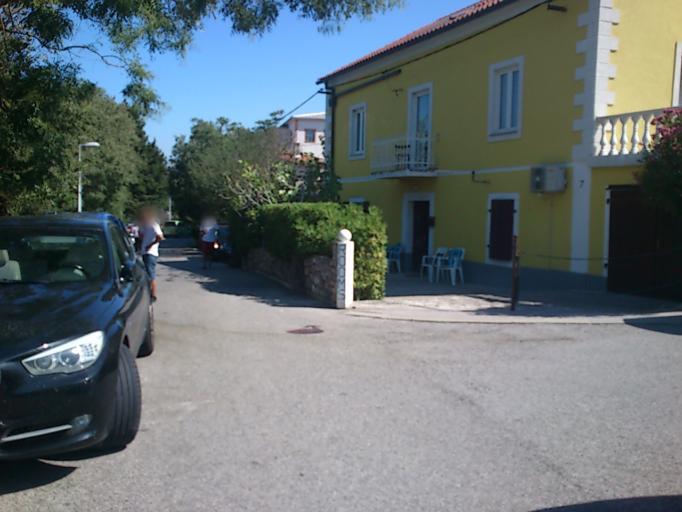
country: HR
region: Licko-Senjska
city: Senj
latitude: 44.9306
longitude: 14.9206
